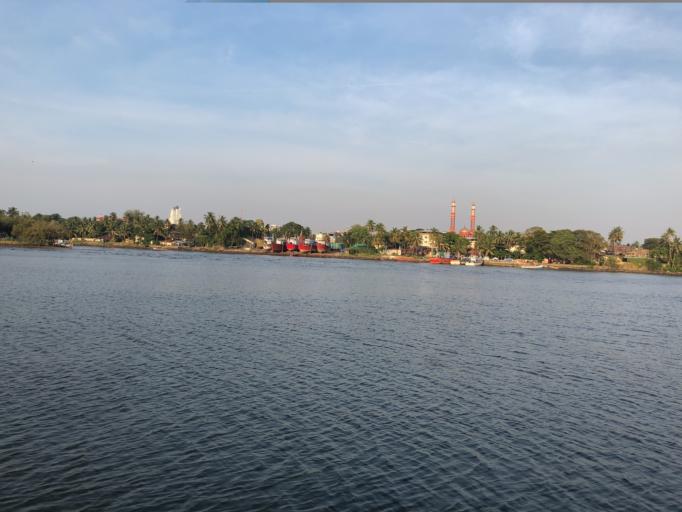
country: IN
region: Karnataka
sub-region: Dakshina Kannada
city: Mangalore
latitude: 12.8757
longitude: 74.8257
